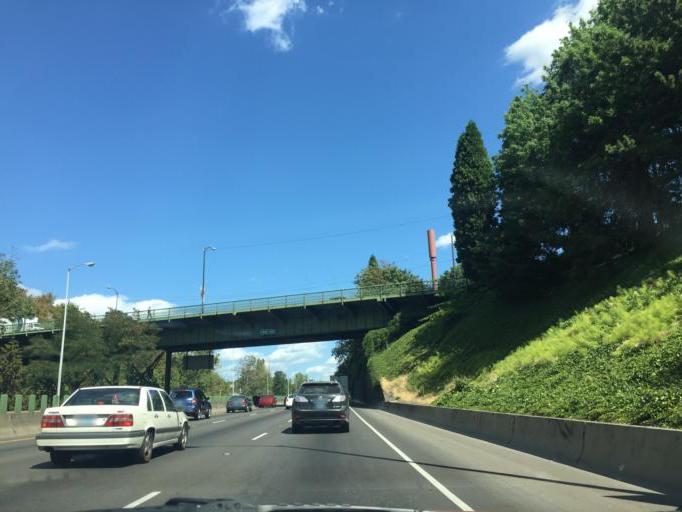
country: US
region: Oregon
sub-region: Multnomah County
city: Portland
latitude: 45.5281
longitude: -122.6546
